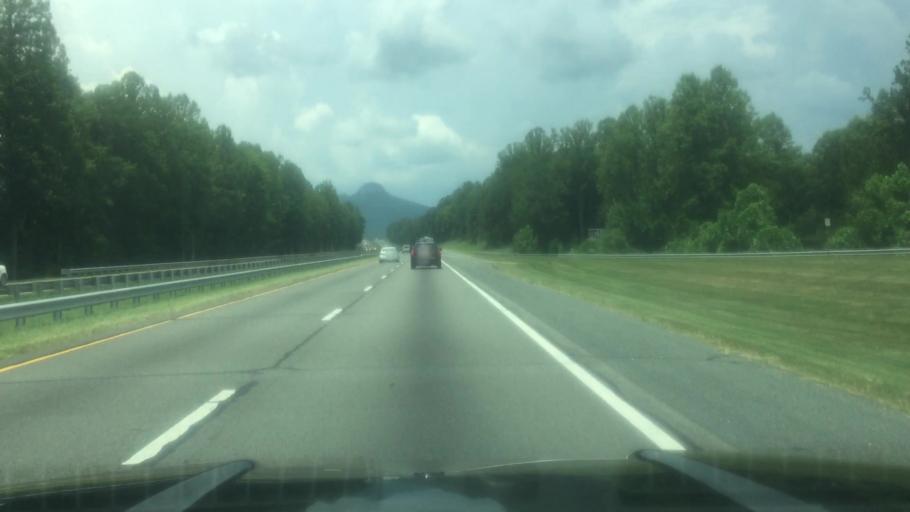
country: US
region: North Carolina
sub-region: Stokes County
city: King
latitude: 36.3075
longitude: -80.4232
